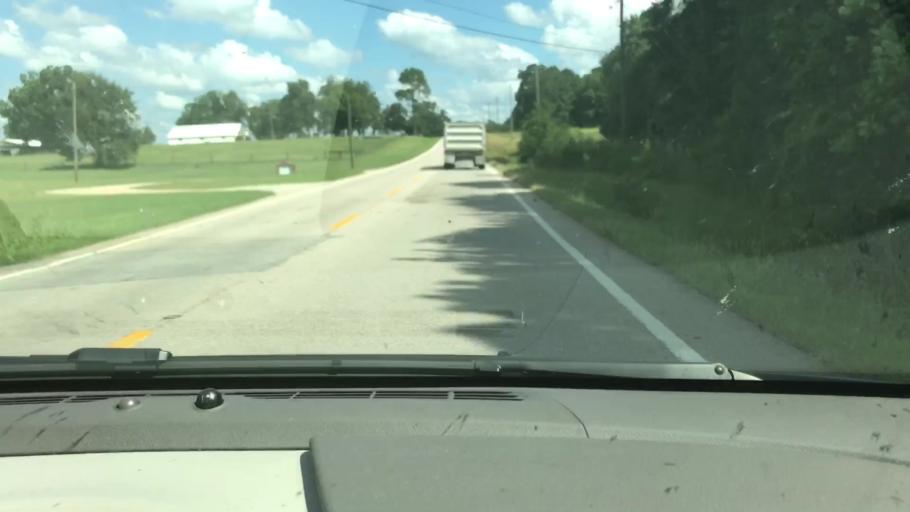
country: US
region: Georgia
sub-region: Troup County
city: West Point
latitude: 32.8754
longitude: -85.0343
